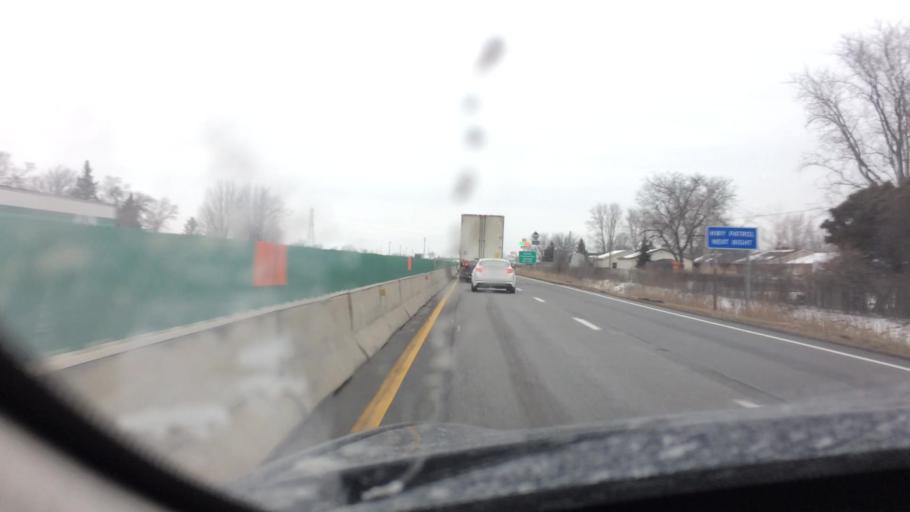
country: US
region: Ohio
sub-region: Hancock County
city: Findlay
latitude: 41.0787
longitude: -83.6598
